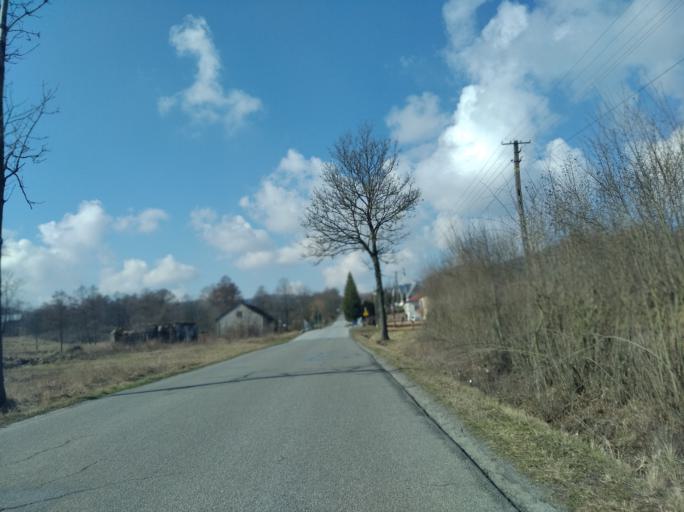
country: PL
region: Subcarpathian Voivodeship
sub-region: Powiat strzyzowski
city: Frysztak
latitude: 49.8729
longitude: 21.5864
